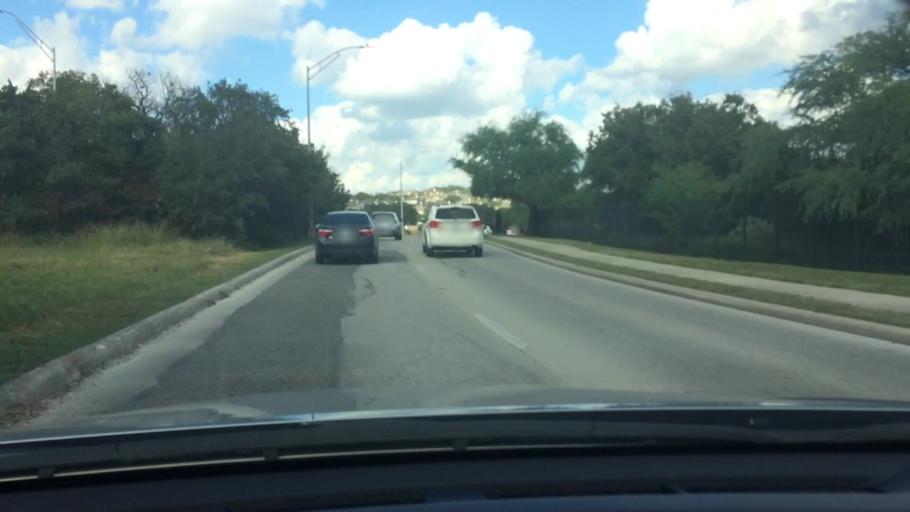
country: US
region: Texas
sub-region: Bexar County
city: Hollywood Park
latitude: 29.6439
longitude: -98.4370
